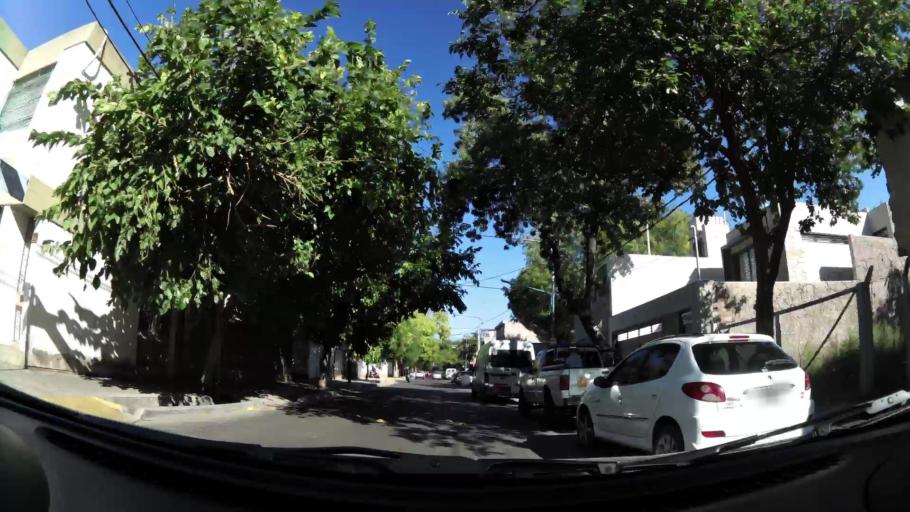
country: AR
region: Mendoza
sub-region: Departamento de Godoy Cruz
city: Godoy Cruz
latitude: -32.9119
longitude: -68.8459
